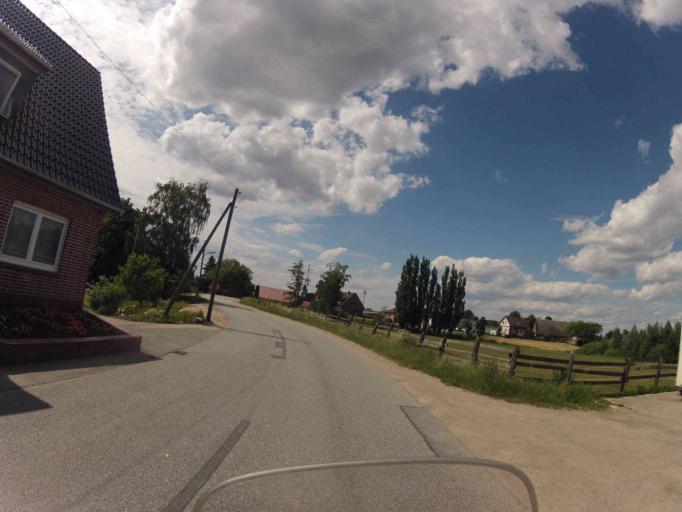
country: DE
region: Hamburg
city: Bergedorf
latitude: 53.4379
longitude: 10.1857
